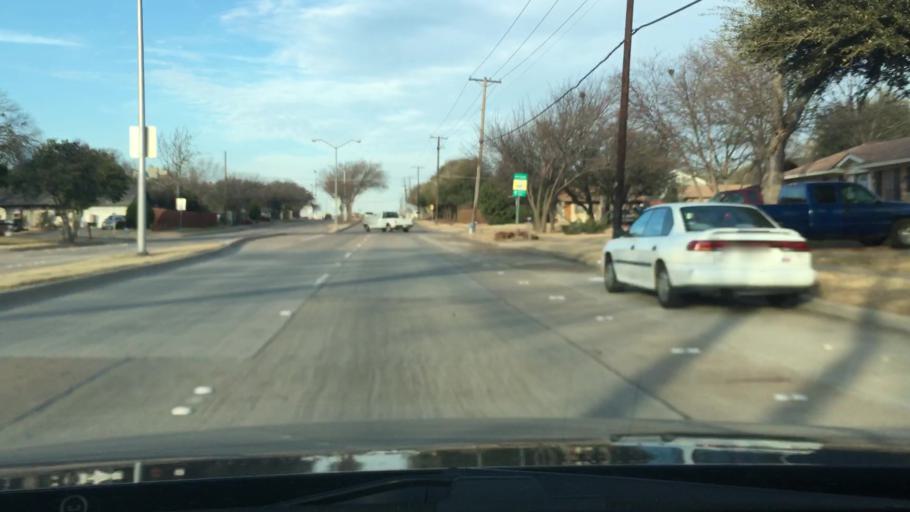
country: US
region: Texas
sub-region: Collin County
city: Plano
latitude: 33.0314
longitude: -96.6943
